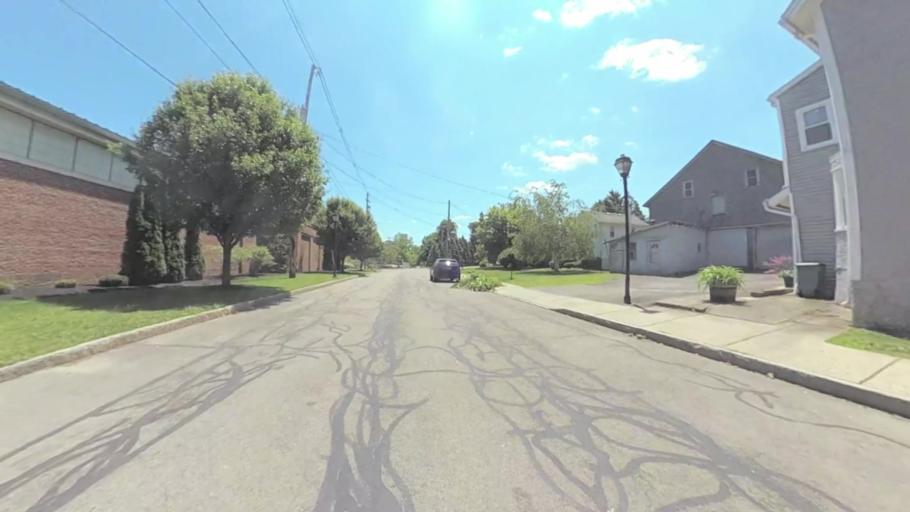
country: US
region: New York
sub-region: Monroe County
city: Fairport
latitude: 43.1009
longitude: -77.4381
